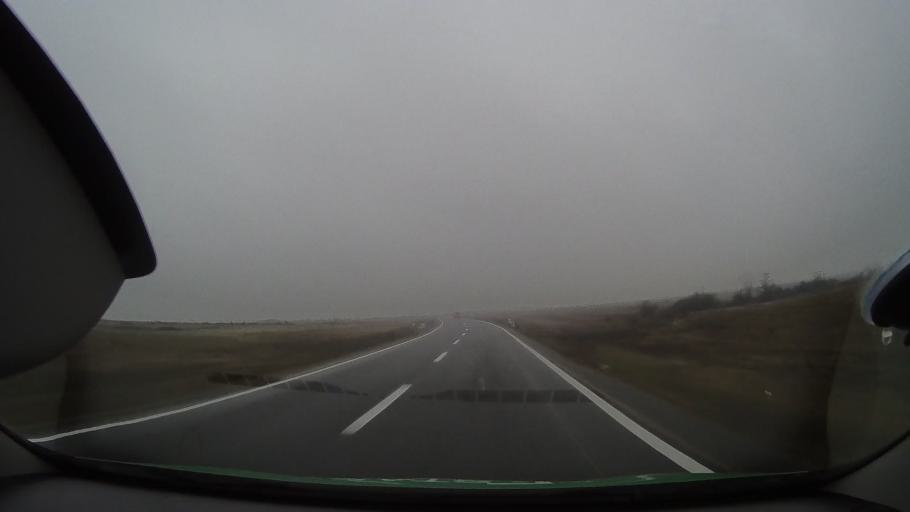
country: RO
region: Arad
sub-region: Comuna Craiova
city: Craiova
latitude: 46.6243
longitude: 21.9585
